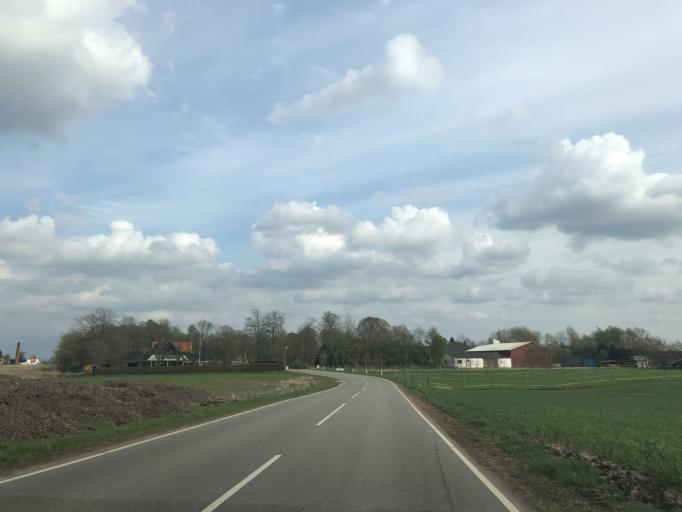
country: DK
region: Zealand
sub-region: Roskilde Kommune
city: Gundsomagle
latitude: 55.7107
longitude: 12.1560
